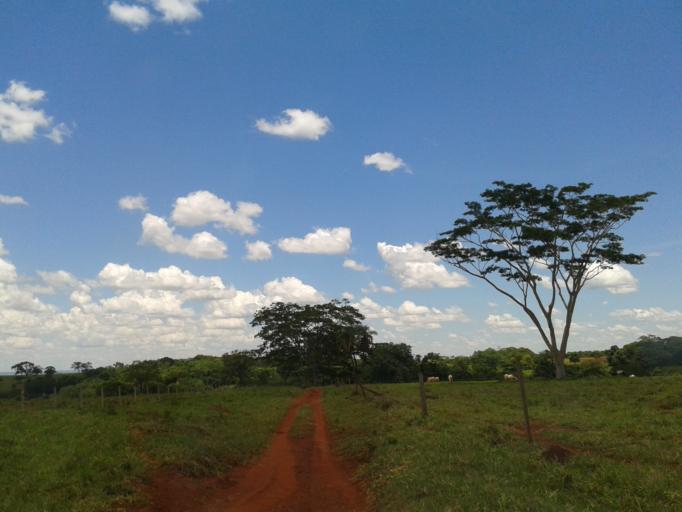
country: BR
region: Minas Gerais
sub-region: Centralina
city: Centralina
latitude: -18.7043
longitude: -49.1763
